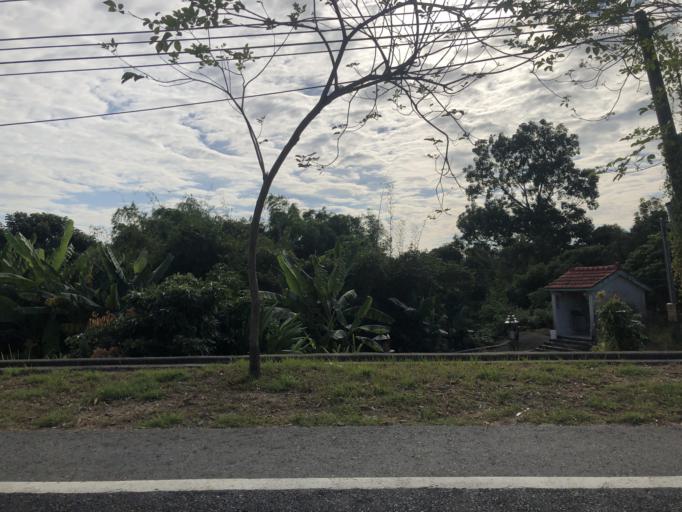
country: TW
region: Taiwan
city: Yujing
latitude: 23.0525
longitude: 120.4171
